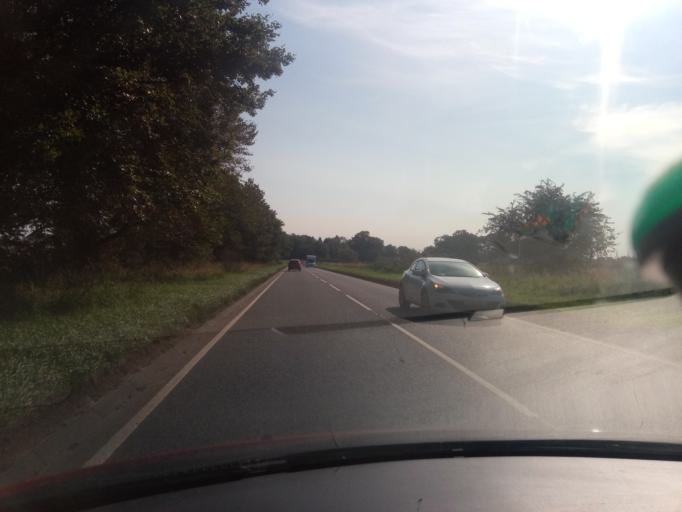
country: GB
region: England
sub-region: North Yorkshire
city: Raskelf
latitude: 54.1707
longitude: -1.2507
